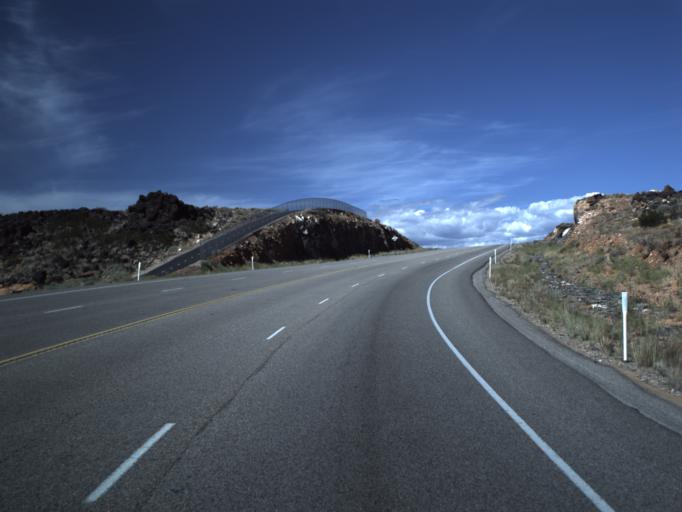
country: US
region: Utah
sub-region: Washington County
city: Santa Clara
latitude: 37.1618
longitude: -113.6099
